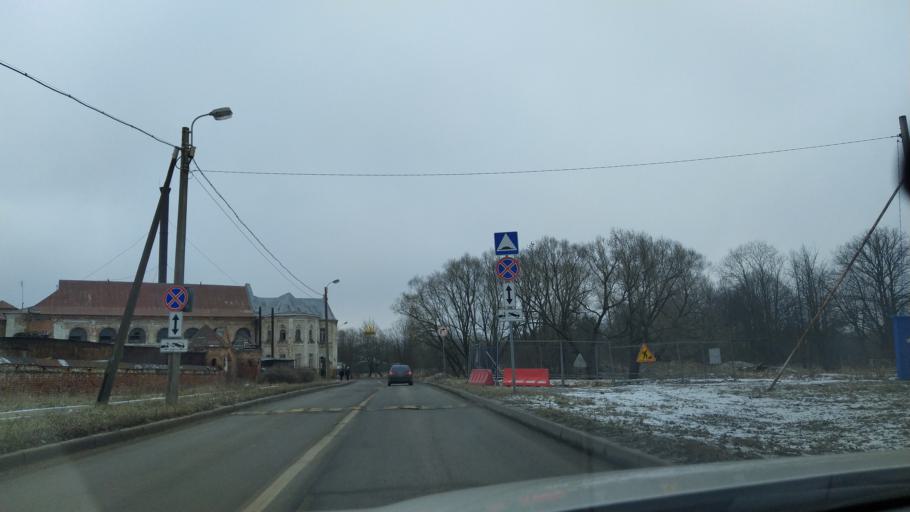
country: RU
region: St.-Petersburg
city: Pushkin
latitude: 59.7296
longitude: 30.3855
